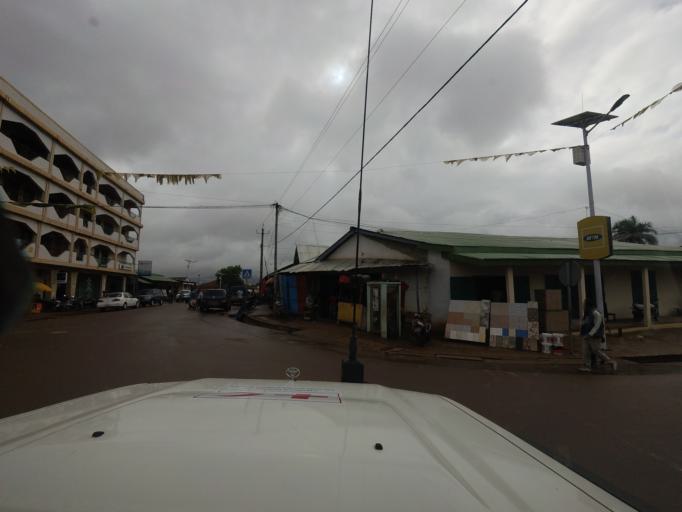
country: GN
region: Nzerekore
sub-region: Nzerekore Prefecture
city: Nzerekore
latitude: 7.7492
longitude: -8.8189
